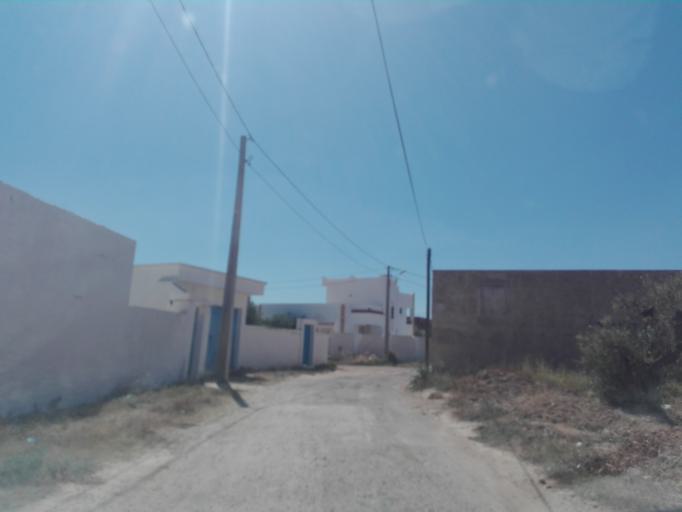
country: TN
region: Safaqis
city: Jabinyanah
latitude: 34.7190
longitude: 11.2424
